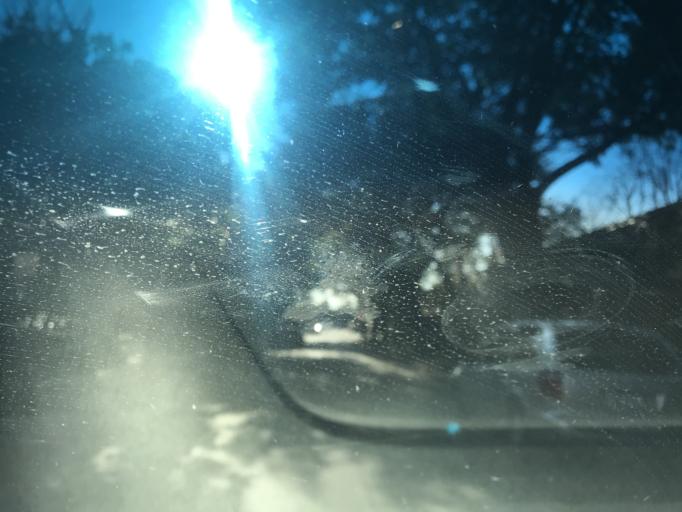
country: US
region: Texas
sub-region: Dallas County
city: Highland Park
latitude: 32.8214
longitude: -96.8129
